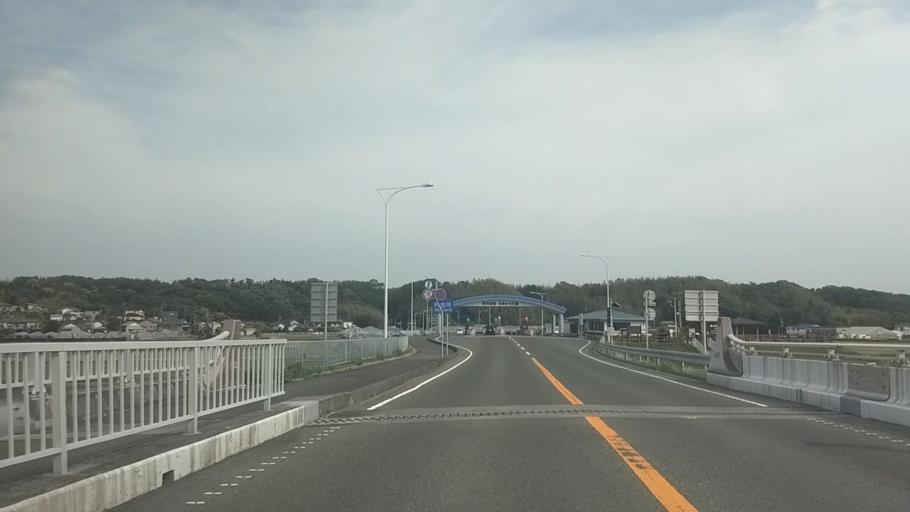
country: JP
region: Shizuoka
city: Kosai-shi
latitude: 34.7274
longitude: 137.6277
